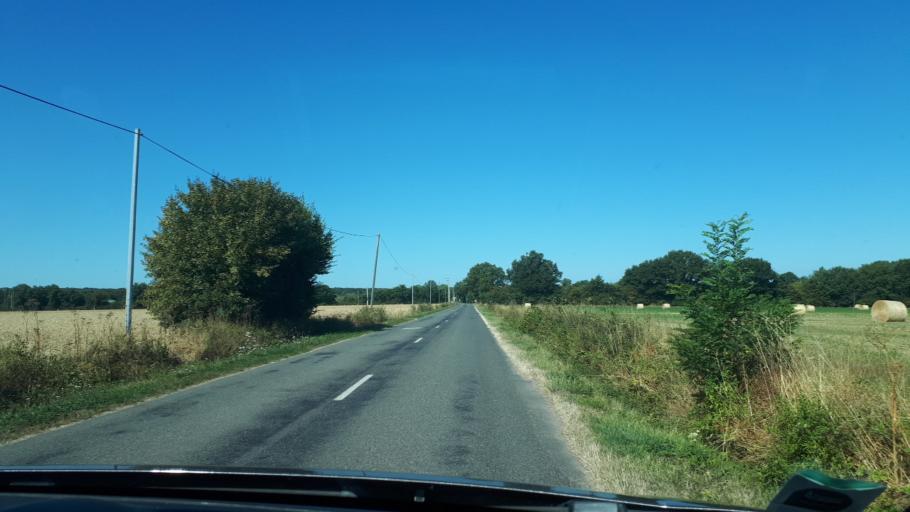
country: FR
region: Centre
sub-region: Departement du Loiret
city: Saint-Brisson-sur-Loire
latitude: 47.5952
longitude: 2.6983
